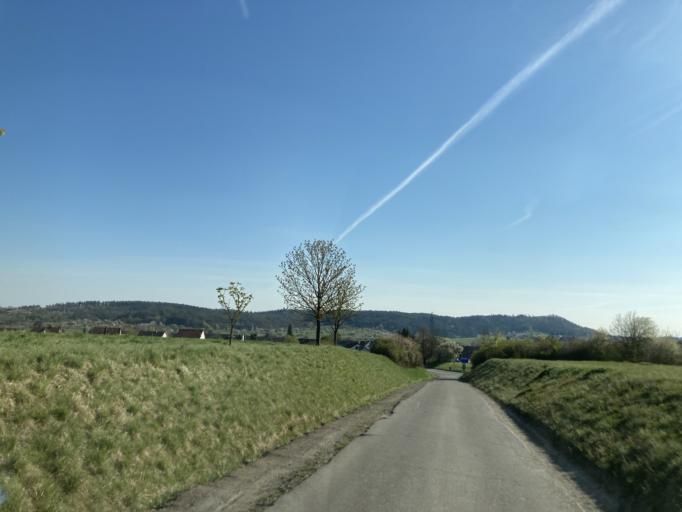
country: DE
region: Baden-Wuerttemberg
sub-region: Tuebingen Region
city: Rottenburg
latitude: 48.5397
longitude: 8.9514
